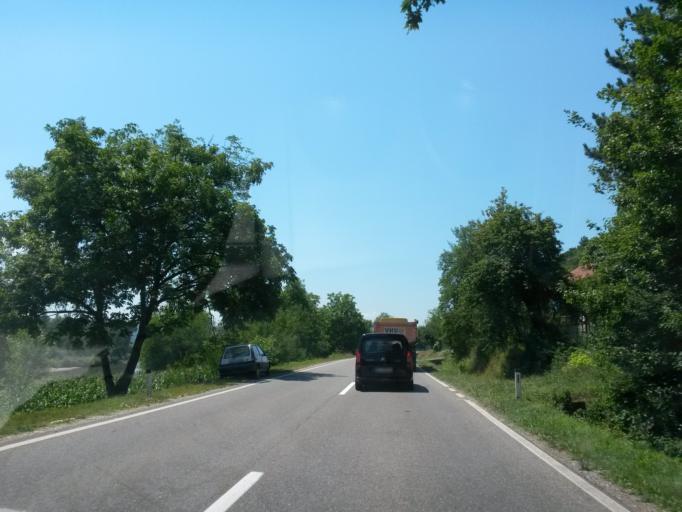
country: BA
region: Federation of Bosnia and Herzegovina
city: Odzak
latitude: 44.9458
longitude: 18.2116
